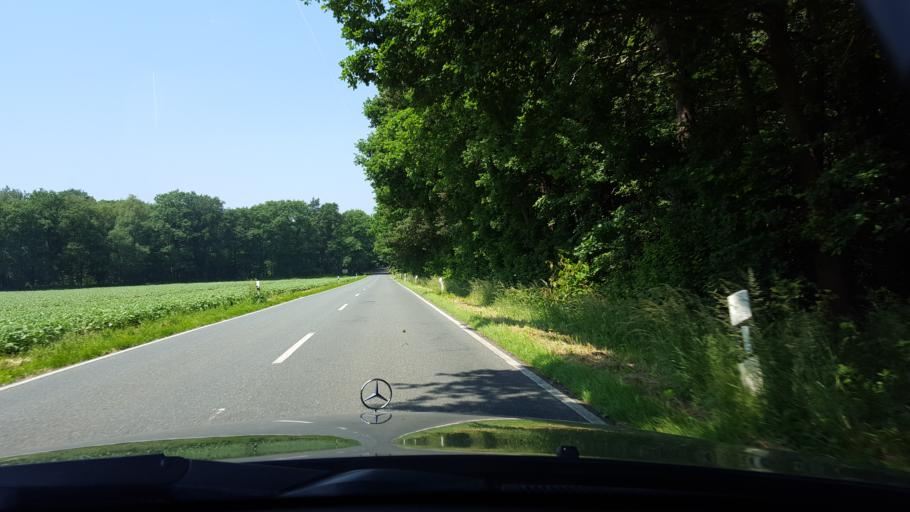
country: DE
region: North Rhine-Westphalia
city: Oer-Erkenschwick
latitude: 51.7265
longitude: 7.2897
